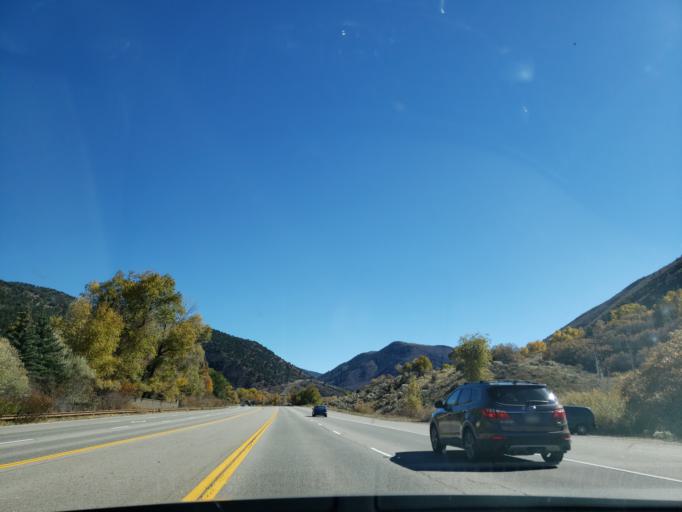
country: US
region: Colorado
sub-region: Eagle County
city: Basalt
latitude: 39.3420
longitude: -107.0045
